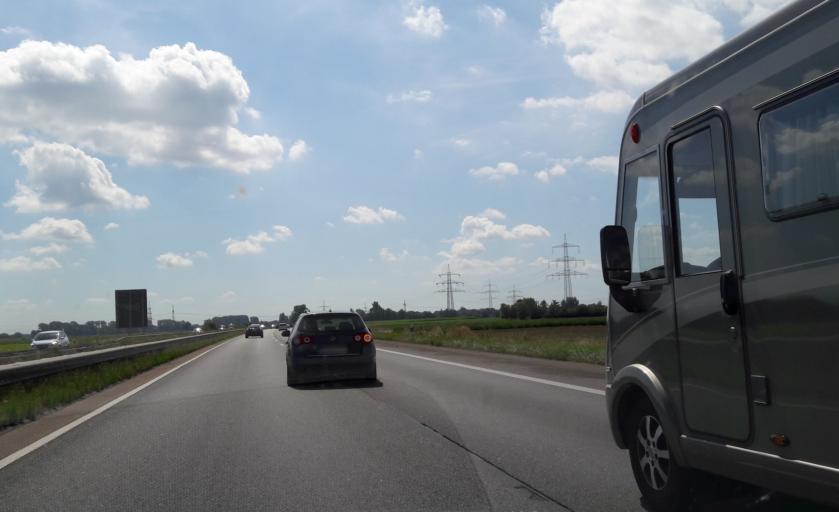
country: DE
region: Rheinland-Pfalz
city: Mutterstadt
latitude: 49.4264
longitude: 8.3358
